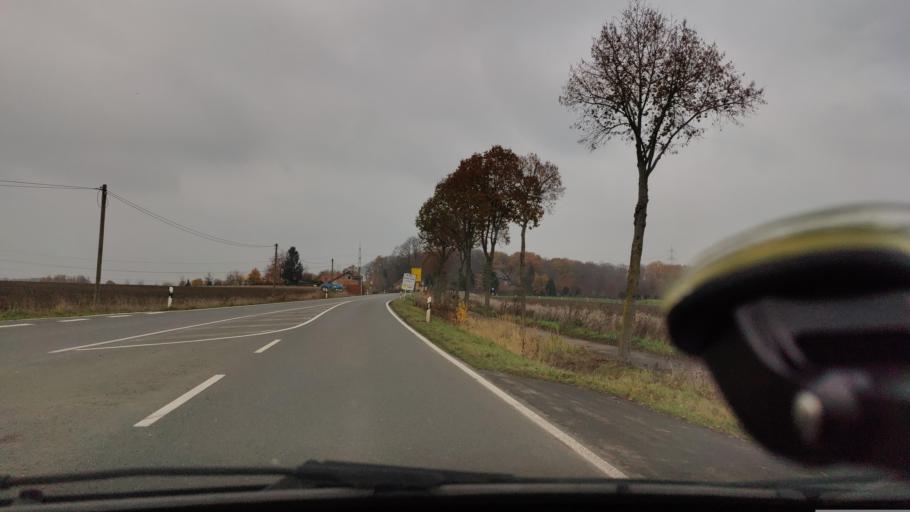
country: DE
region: North Rhine-Westphalia
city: Lunen
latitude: 51.6538
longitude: 7.5027
